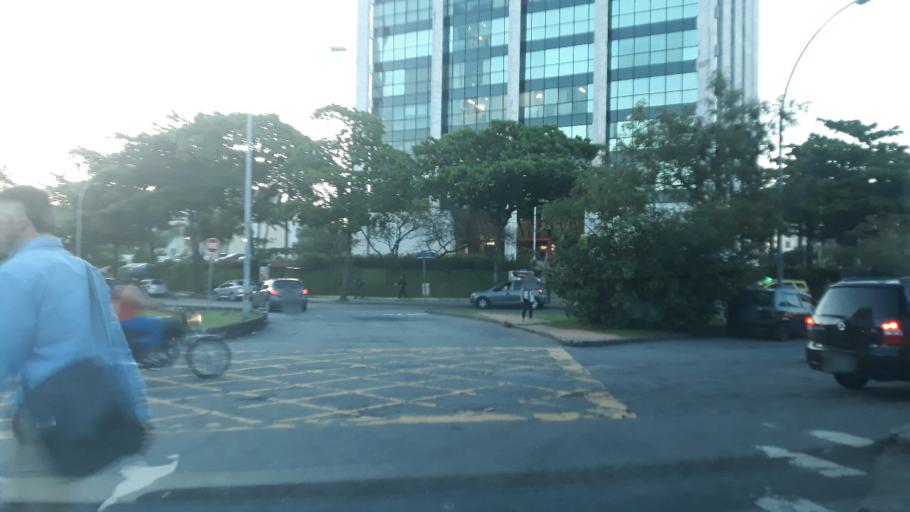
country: BR
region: Rio de Janeiro
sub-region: Rio De Janeiro
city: Rio de Janeiro
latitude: -23.0012
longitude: -43.3472
